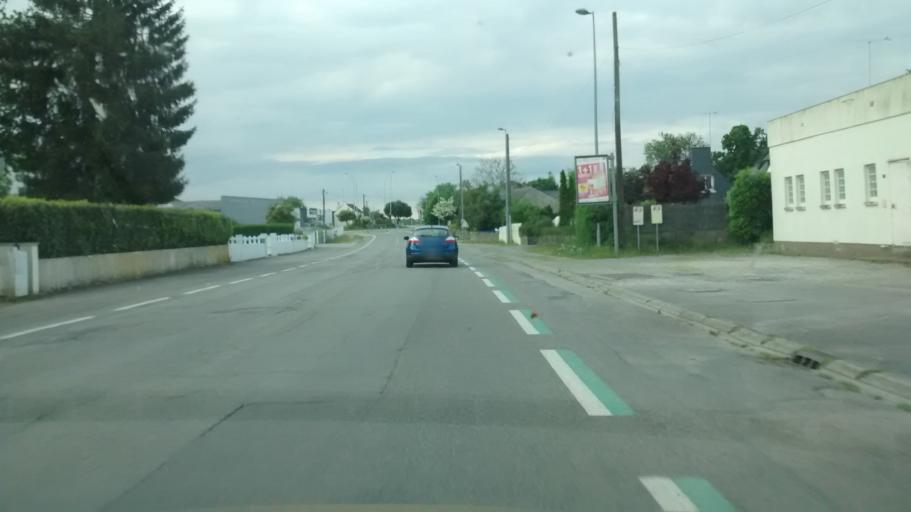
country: FR
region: Brittany
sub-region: Departement du Morbihan
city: Questembert
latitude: 47.6665
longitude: -2.4498
